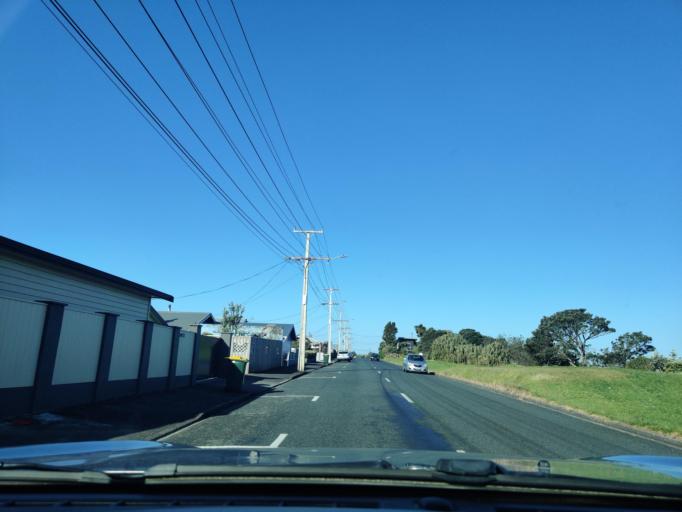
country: NZ
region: Taranaki
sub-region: New Plymouth District
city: New Plymouth
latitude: -39.0479
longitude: 174.1066
